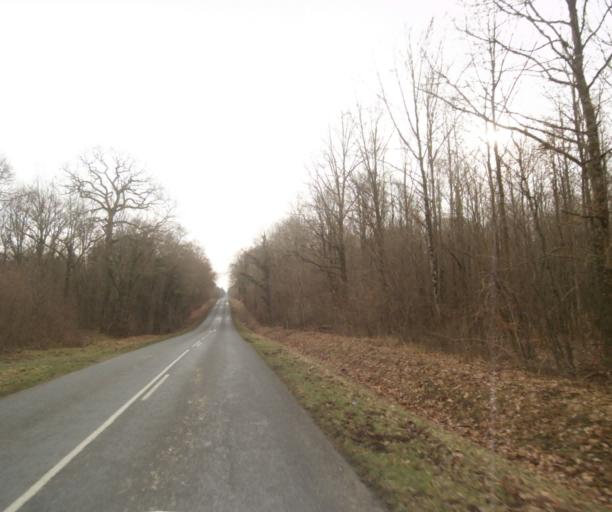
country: FR
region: Champagne-Ardenne
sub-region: Departement de la Marne
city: Pargny-sur-Saulx
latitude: 48.7269
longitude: 4.8691
